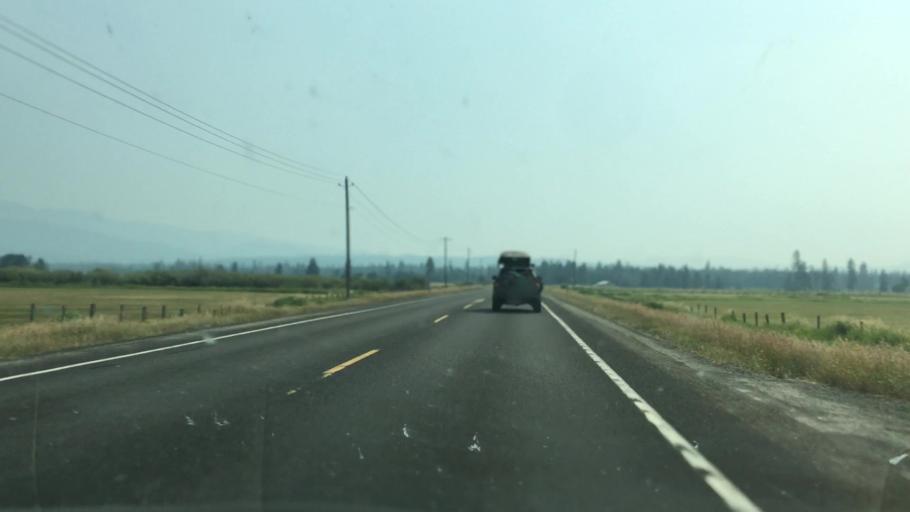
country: US
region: Idaho
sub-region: Valley County
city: Cascade
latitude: 44.4201
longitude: -115.9998
